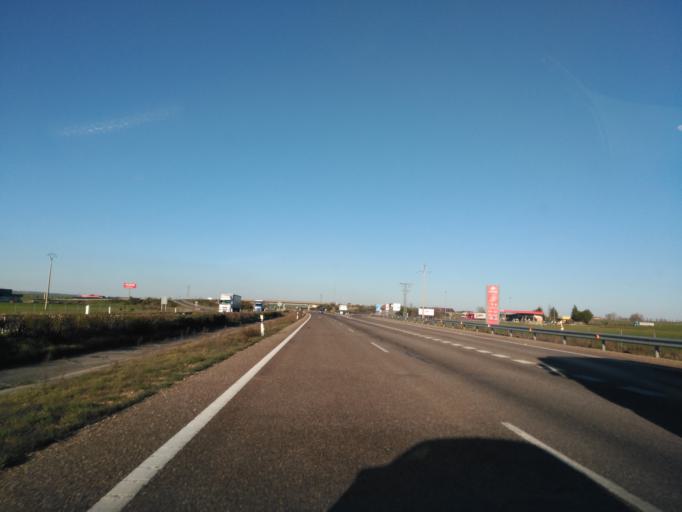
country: ES
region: Castille and Leon
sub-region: Provincia de Salamanca
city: Pedrosillo el Ralo
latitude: 41.0539
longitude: -5.5474
